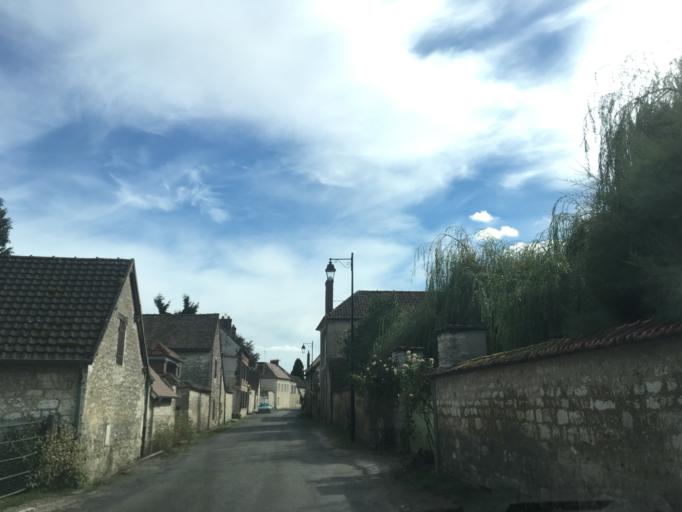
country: FR
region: Haute-Normandie
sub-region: Departement de l'Eure
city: Saint-Just
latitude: 49.1224
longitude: 1.4359
